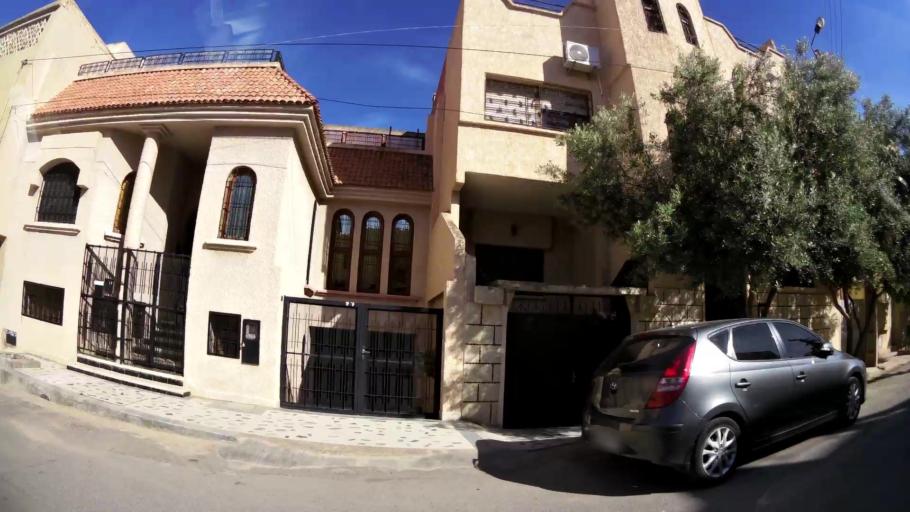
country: MA
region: Oriental
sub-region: Oujda-Angad
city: Oujda
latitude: 34.6683
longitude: -1.9141
